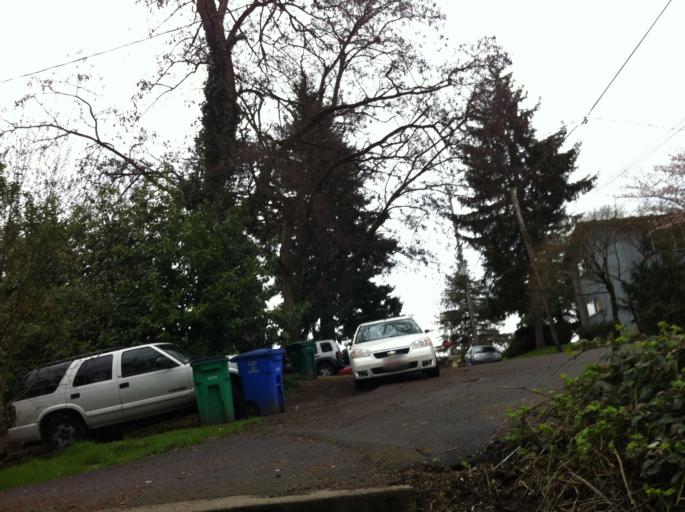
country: US
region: Oregon
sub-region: Multnomah County
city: Lents
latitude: 45.5342
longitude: -122.5745
